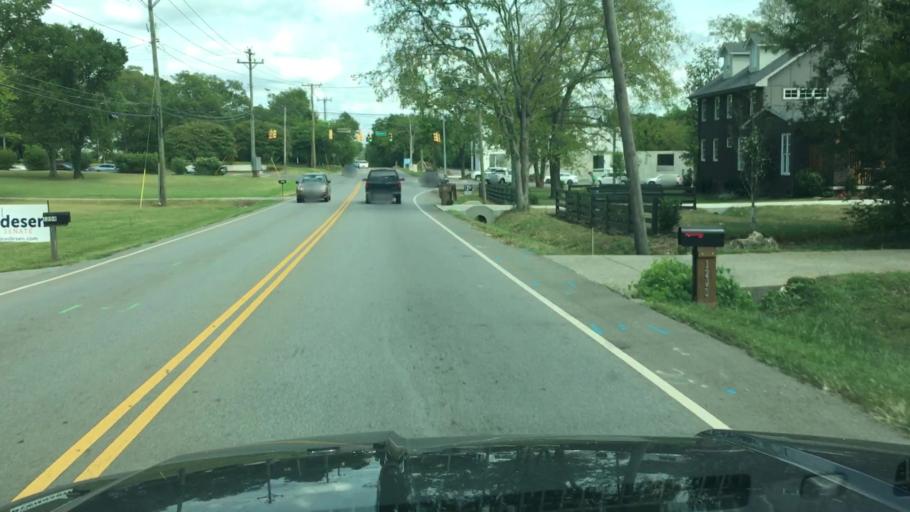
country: US
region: Tennessee
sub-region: Davidson County
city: Oak Hill
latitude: 36.0895
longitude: -86.8041
